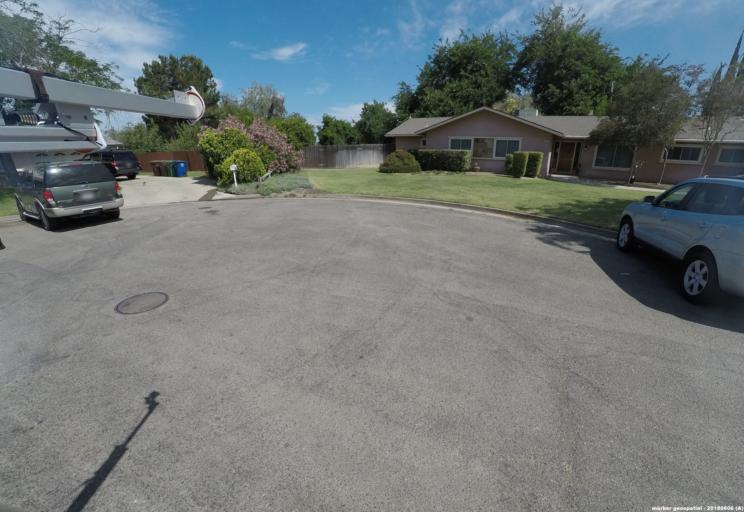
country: US
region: California
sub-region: Fresno County
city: Firebaugh
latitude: 36.8576
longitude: -120.4376
